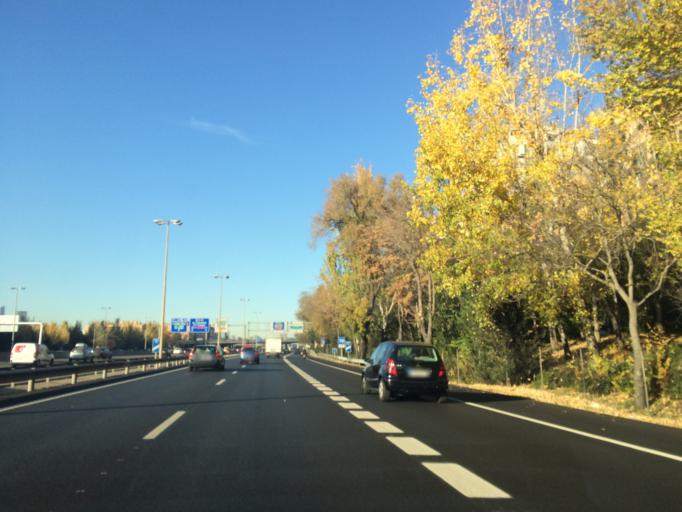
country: ES
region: Madrid
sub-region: Provincia de Madrid
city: Ciudad Lineal
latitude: 40.4493
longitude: -3.6620
